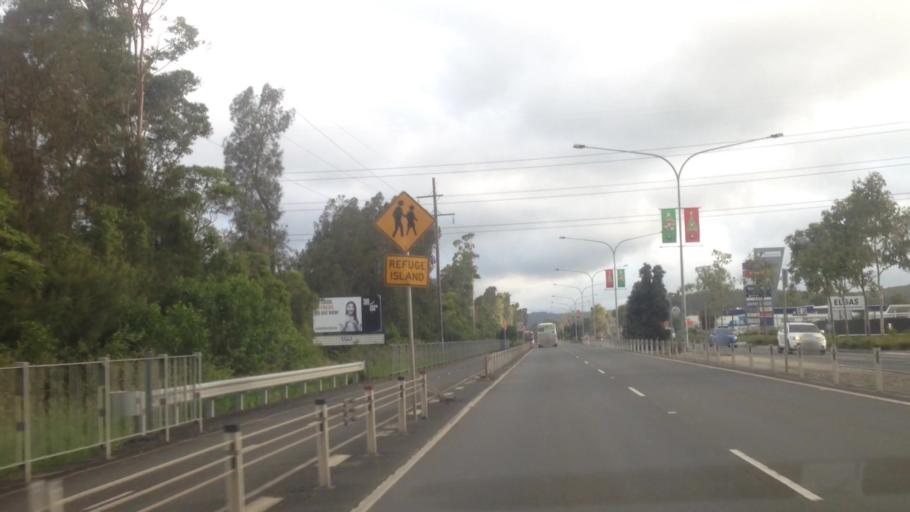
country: AU
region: New South Wales
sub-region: Wyong Shire
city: Chittaway Bay
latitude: -33.2987
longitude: 151.4219
